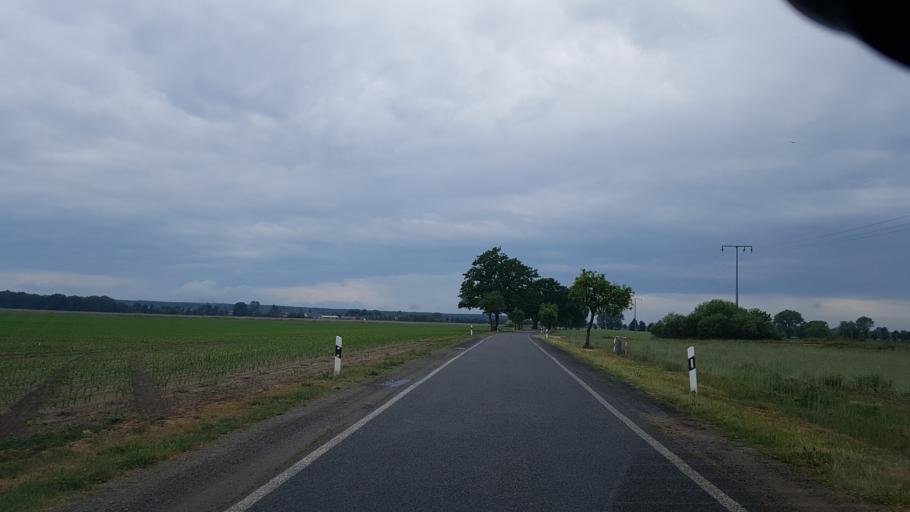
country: DE
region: Brandenburg
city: Schlieben
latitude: 51.6917
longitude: 13.3707
